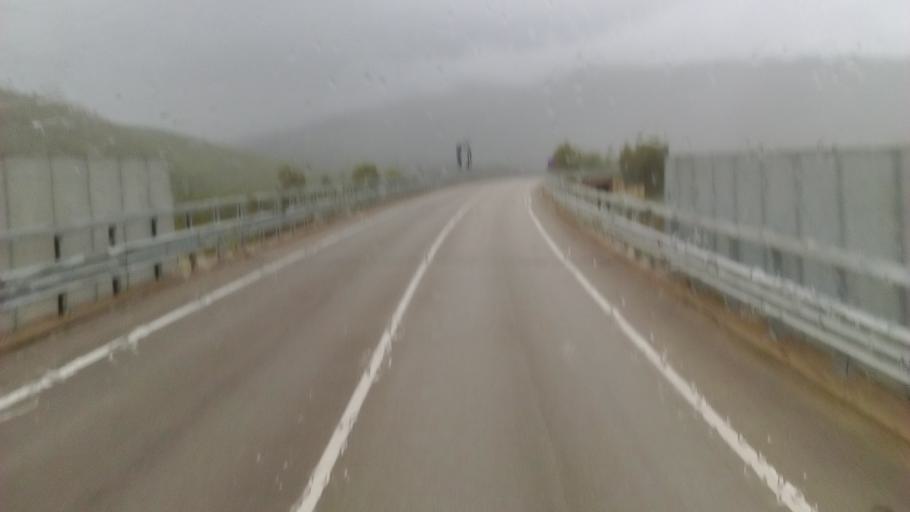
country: IT
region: Sicily
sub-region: Enna
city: Villarosa
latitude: 37.5329
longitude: 14.1298
